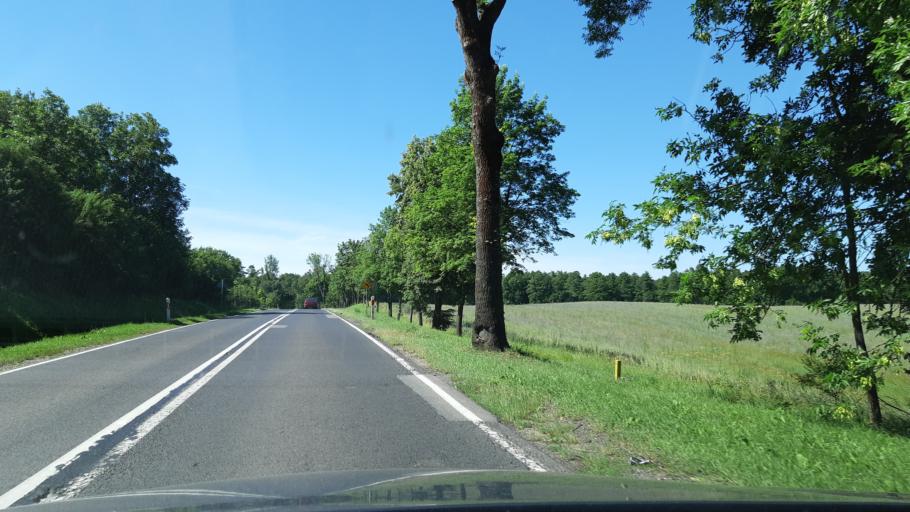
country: PL
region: Warmian-Masurian Voivodeship
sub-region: Powiat mragowski
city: Mragowo
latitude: 53.8350
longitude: 21.3092
